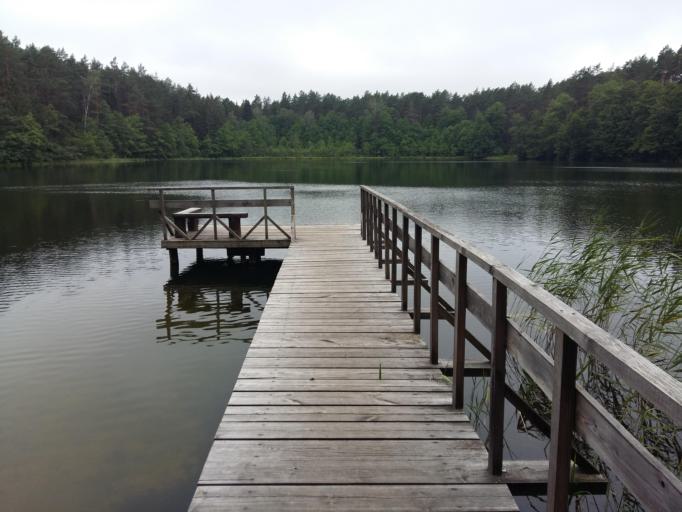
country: LT
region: Alytaus apskritis
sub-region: Alytus
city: Alytus
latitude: 54.1899
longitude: 24.1494
